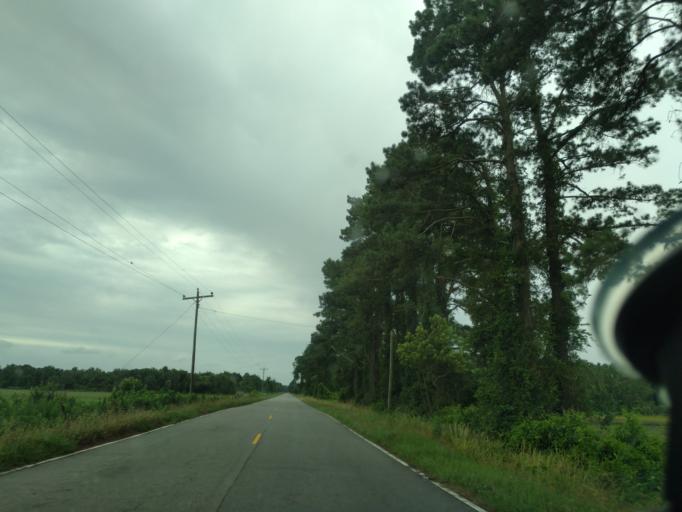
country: US
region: North Carolina
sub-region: Washington County
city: Plymouth
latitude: 35.8072
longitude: -76.5163
